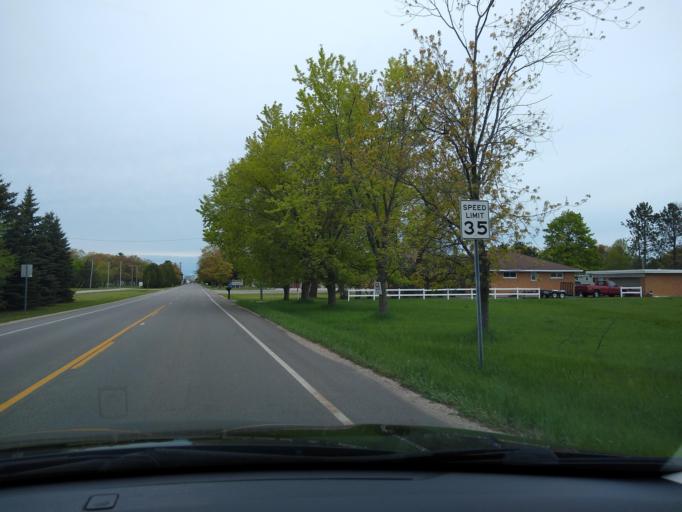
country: US
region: Michigan
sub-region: Delta County
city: Escanaba
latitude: 45.7843
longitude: -87.0769
